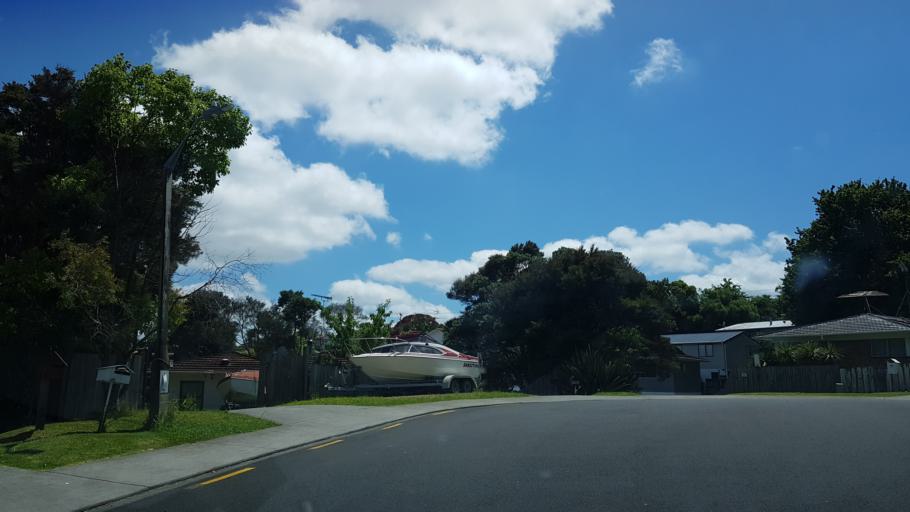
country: NZ
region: Auckland
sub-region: Auckland
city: North Shore
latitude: -36.7883
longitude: 174.7150
